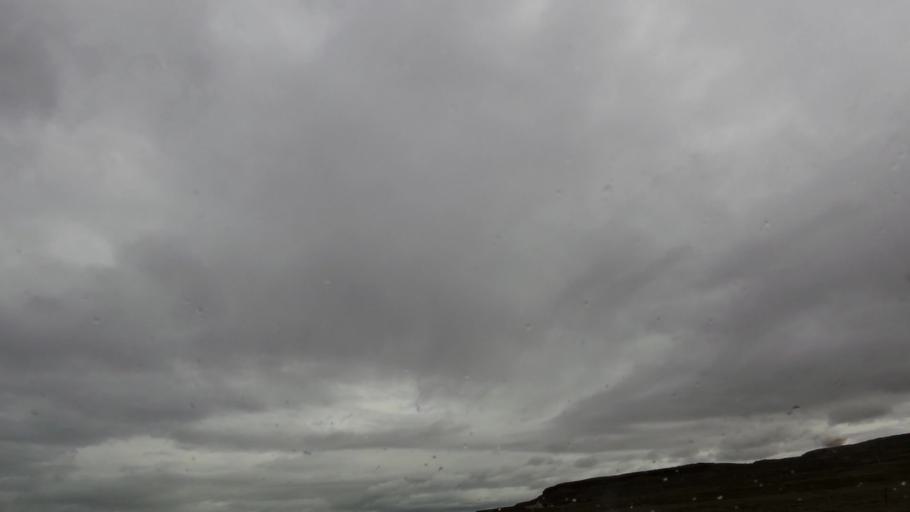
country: IS
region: West
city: Borgarnes
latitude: 65.0248
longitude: -22.1089
